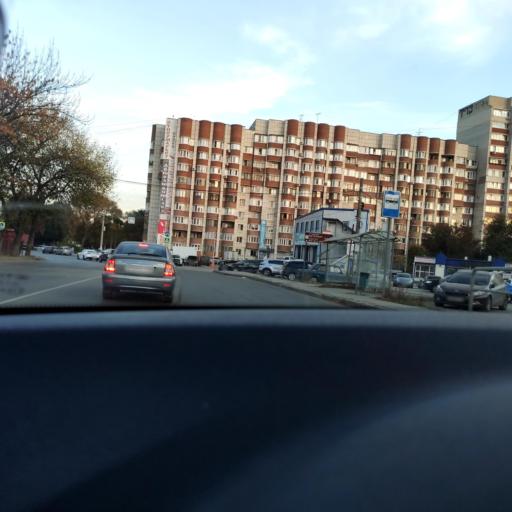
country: RU
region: Samara
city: Petra-Dubrava
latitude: 53.2407
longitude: 50.2747
